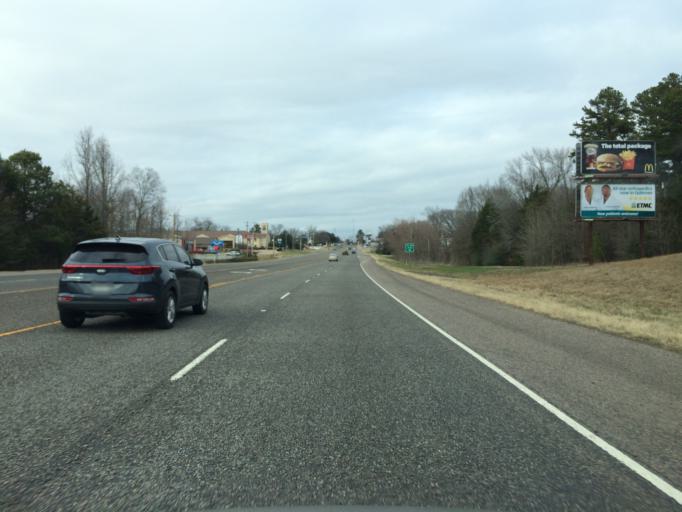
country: US
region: Texas
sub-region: Wood County
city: Mineola
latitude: 32.6468
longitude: -95.4900
